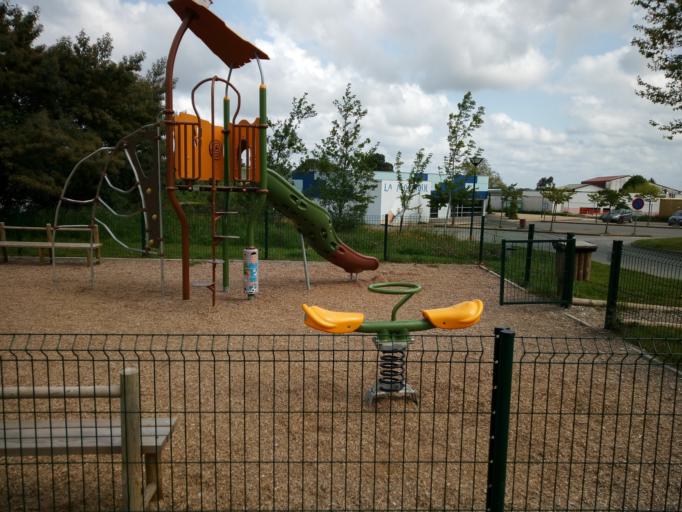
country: FR
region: Aquitaine
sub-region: Departement des Landes
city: Saint-Andre-de-Seignanx
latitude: 43.5584
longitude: -1.3544
